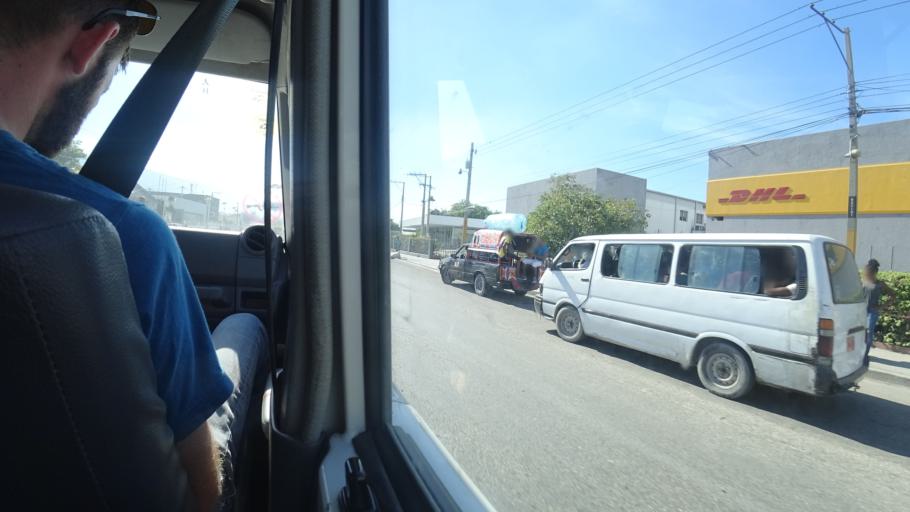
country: HT
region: Ouest
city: Delmas 73
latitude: 18.5679
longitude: -72.3113
